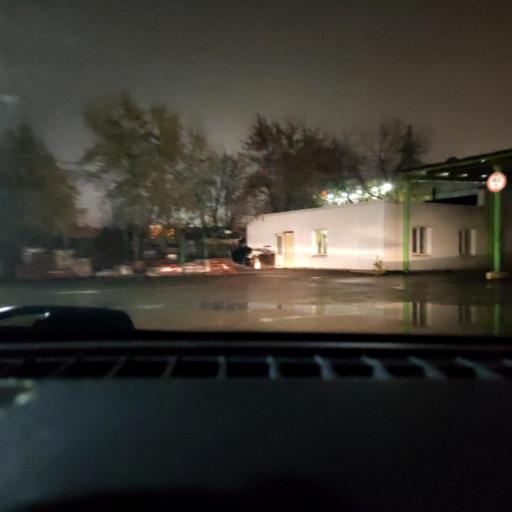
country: RU
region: Perm
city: Kondratovo
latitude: 58.0052
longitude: 56.1505
